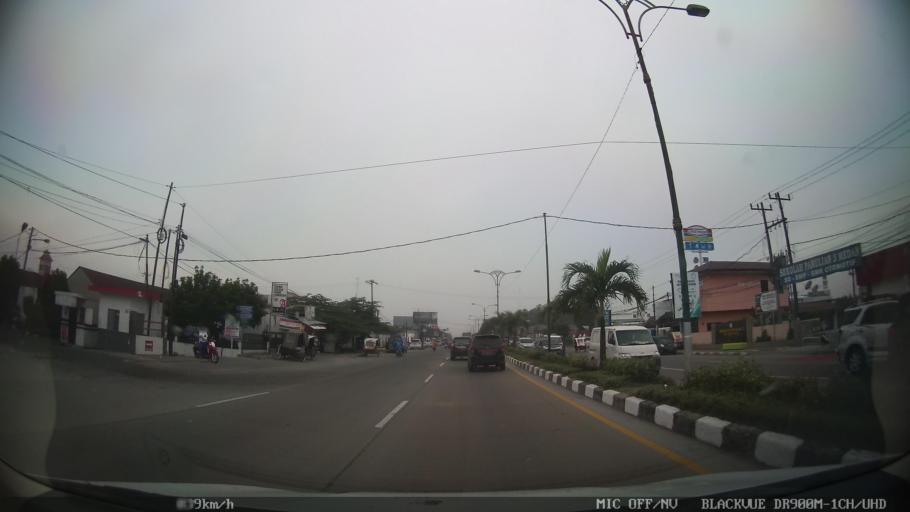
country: ID
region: North Sumatra
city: Deli Tua
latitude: 3.5376
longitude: 98.7097
